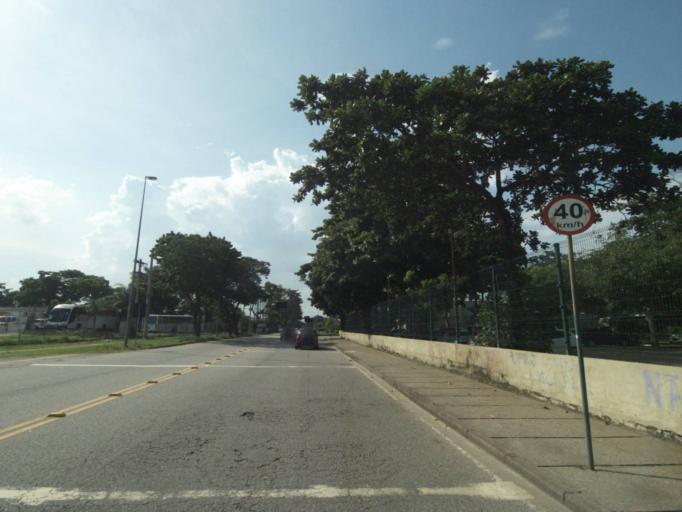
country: BR
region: Rio de Janeiro
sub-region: Rio De Janeiro
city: Rio de Janeiro
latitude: -22.8574
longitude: -43.2343
